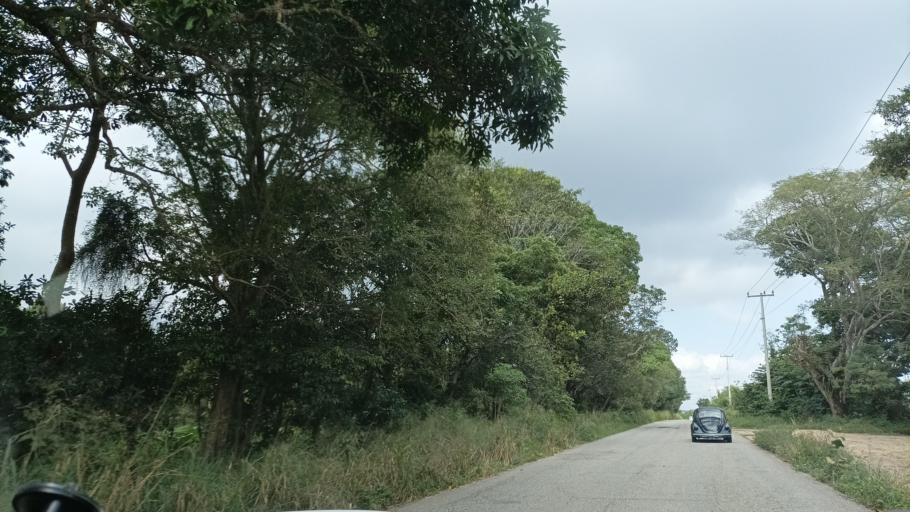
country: MX
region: Veracruz
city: Las Choapas
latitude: 17.8246
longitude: -94.1083
